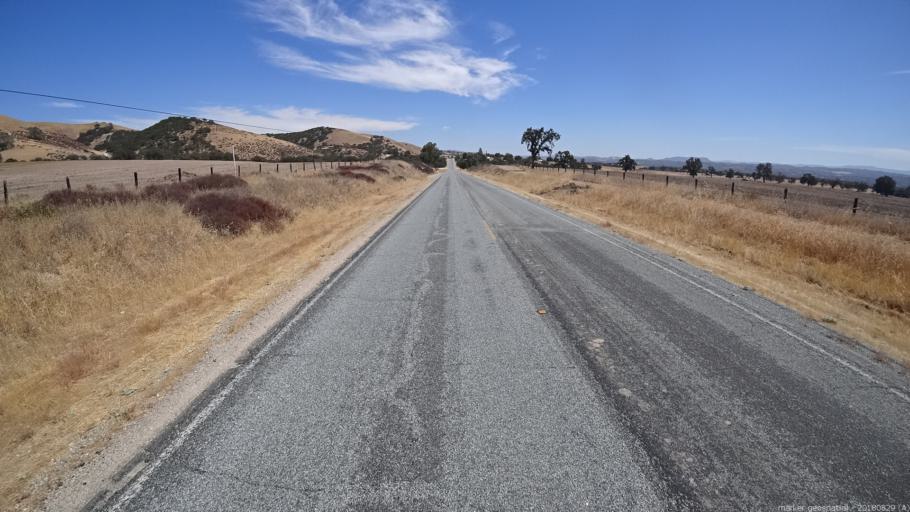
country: US
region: California
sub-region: San Luis Obispo County
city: Lake Nacimiento
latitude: 35.9205
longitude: -121.0344
